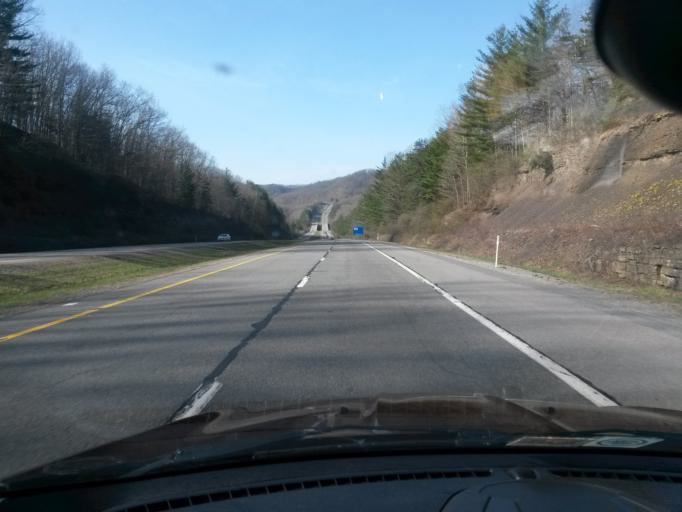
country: US
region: West Virginia
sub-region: Fayette County
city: Mount Hope
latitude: 37.9028
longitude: -81.1754
